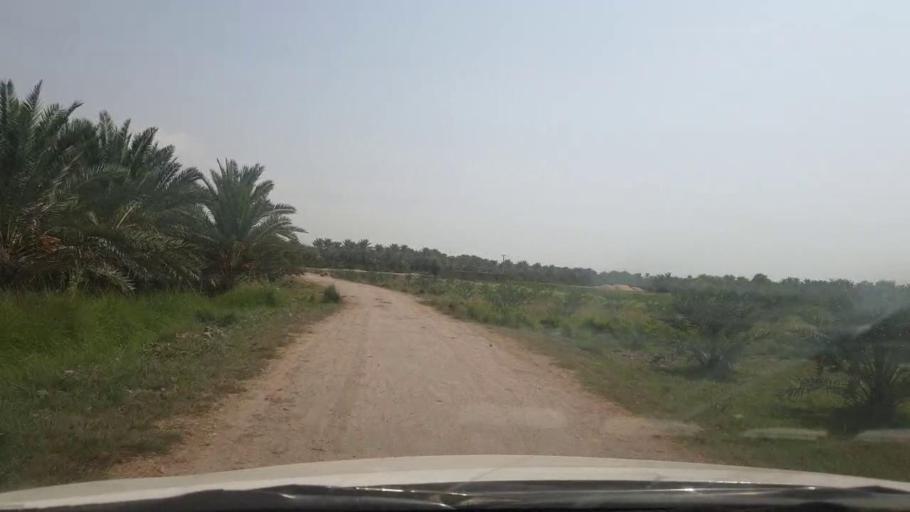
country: PK
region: Sindh
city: Khairpur
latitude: 27.5554
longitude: 68.8389
